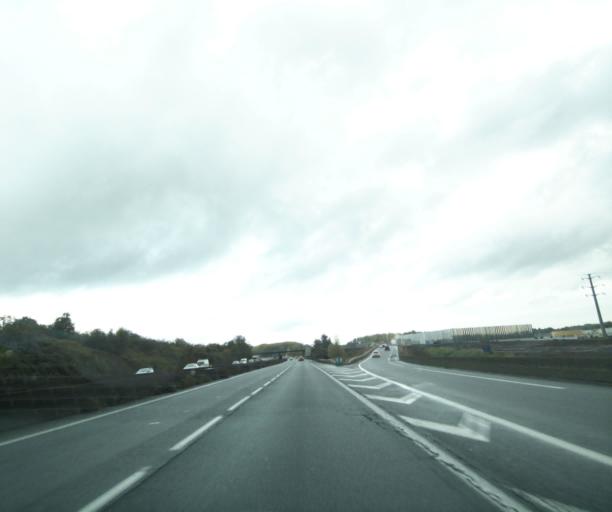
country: FR
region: Nord-Pas-de-Calais
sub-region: Departement du Nord
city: Roncq
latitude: 50.7420
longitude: 3.1374
